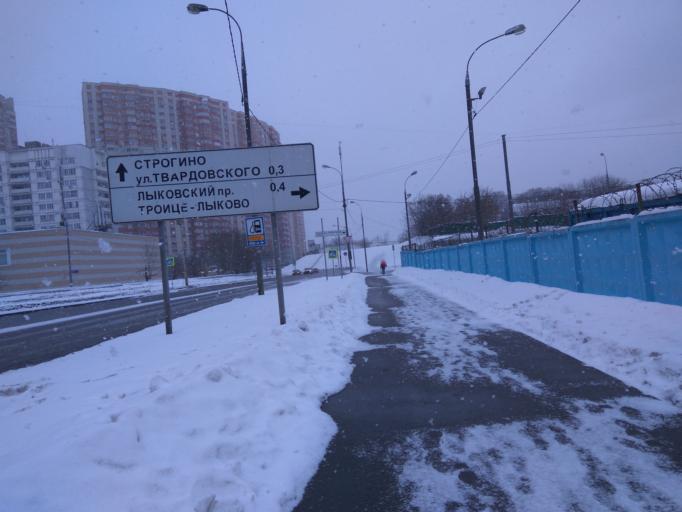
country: RU
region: Moscow
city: Strogino
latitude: 55.7924
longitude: 37.3940
